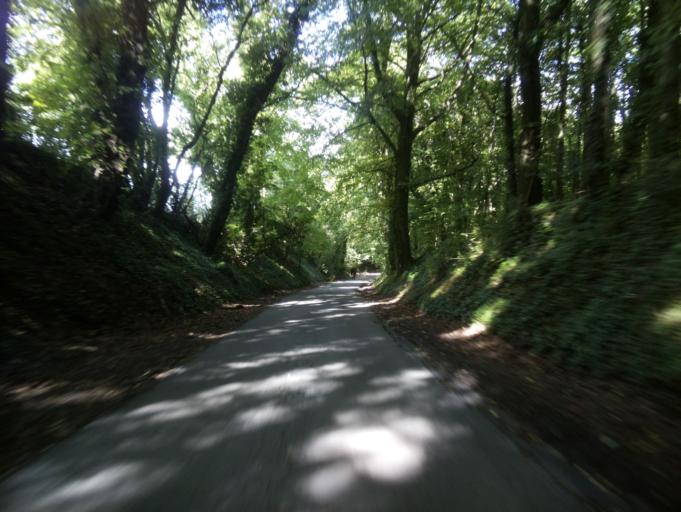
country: GB
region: England
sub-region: Wiltshire
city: Erlestoke
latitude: 51.2778
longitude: -2.0658
